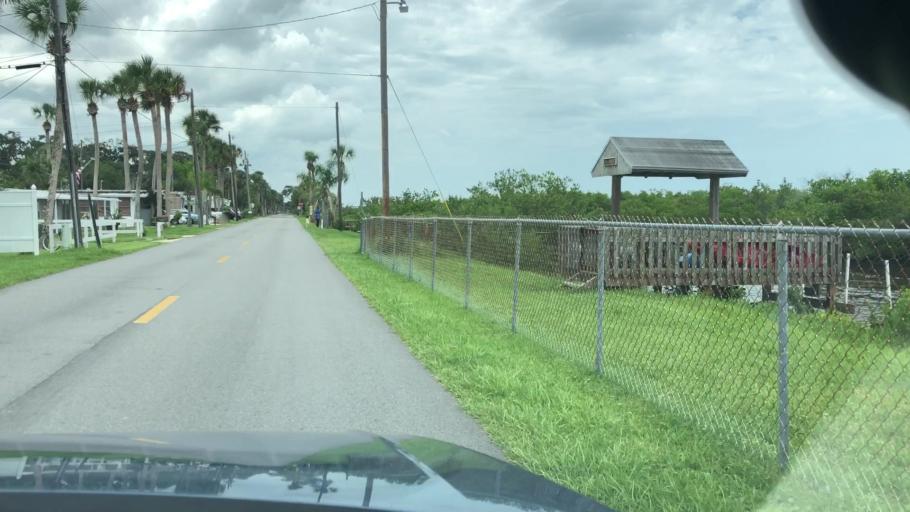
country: US
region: Florida
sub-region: Volusia County
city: Port Orange
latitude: 29.1244
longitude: -80.9760
